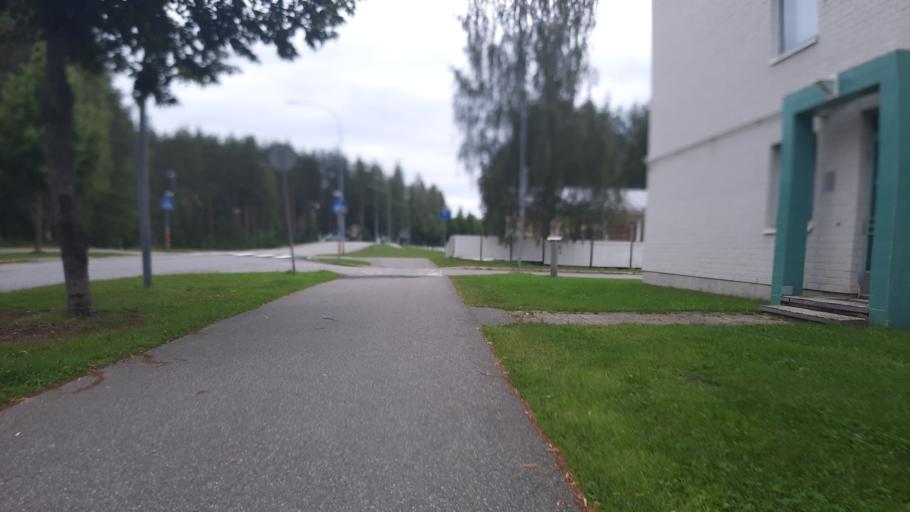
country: FI
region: North Karelia
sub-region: Joensuu
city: Joensuu
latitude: 62.6229
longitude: 29.8564
